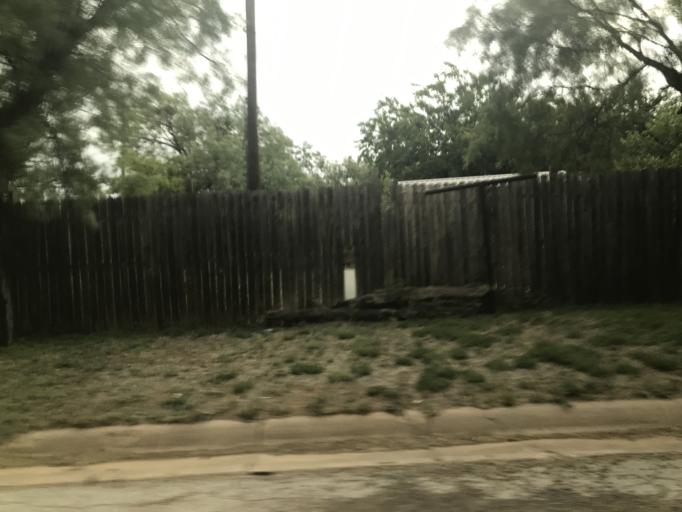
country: US
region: Texas
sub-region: Taylor County
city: Abilene
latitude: 32.4487
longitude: -99.7555
